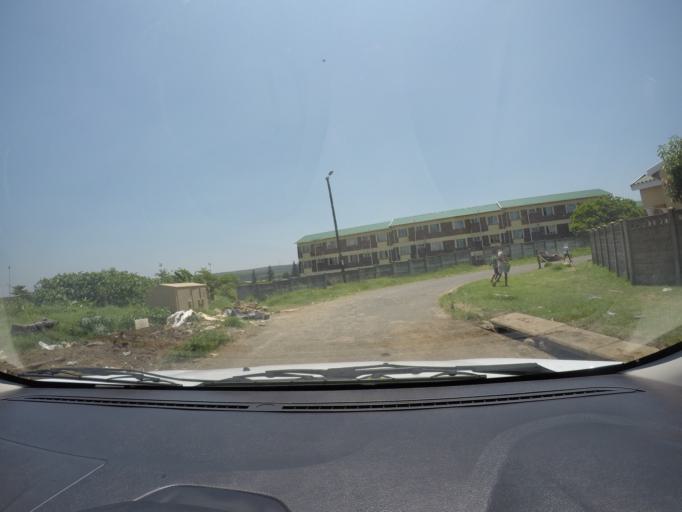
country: ZA
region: KwaZulu-Natal
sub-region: uThungulu District Municipality
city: eSikhawini
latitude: -28.8785
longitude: 31.8980
